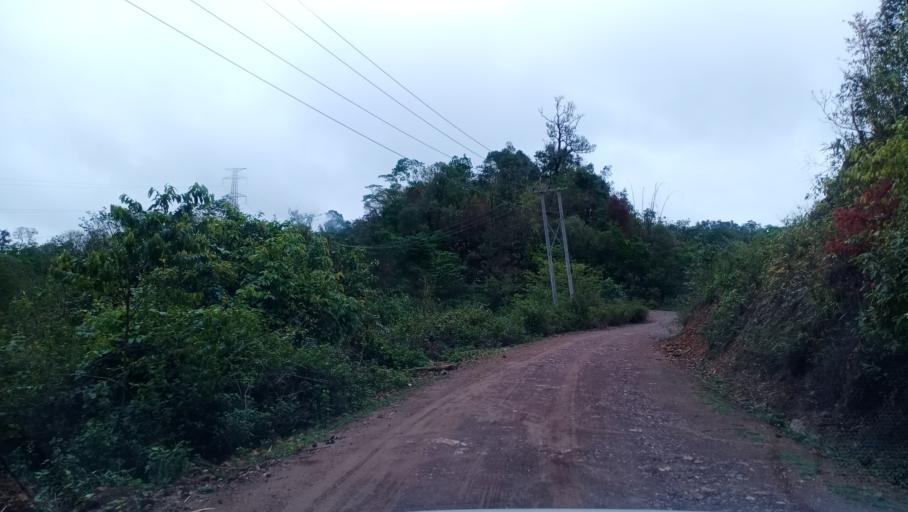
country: LA
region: Phongsali
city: Phongsali
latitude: 21.3437
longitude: 102.0894
